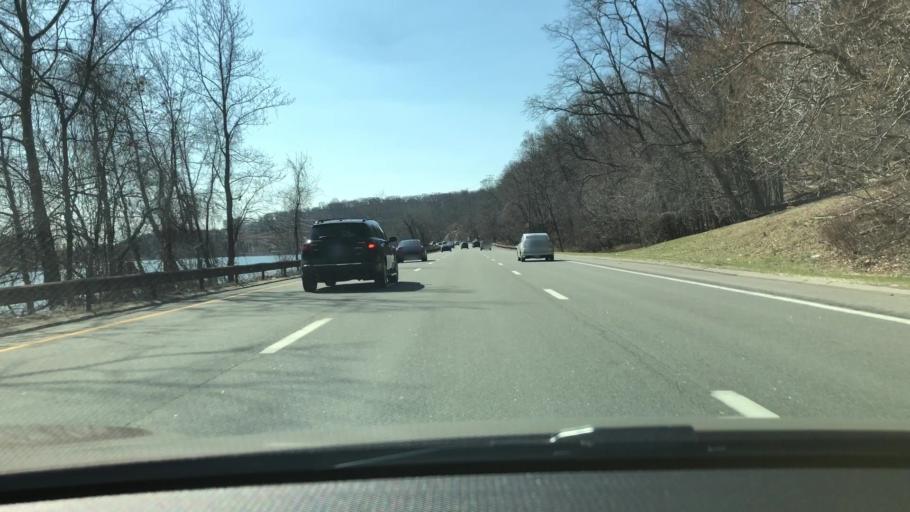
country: US
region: New York
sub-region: Westchester County
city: Greenville
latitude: 40.9781
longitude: -73.8491
